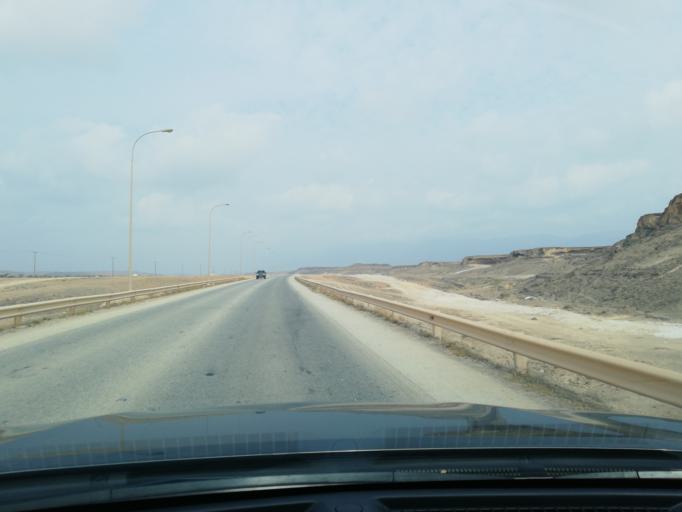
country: OM
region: Zufar
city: Salalah
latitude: 16.9539
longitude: 53.9193
